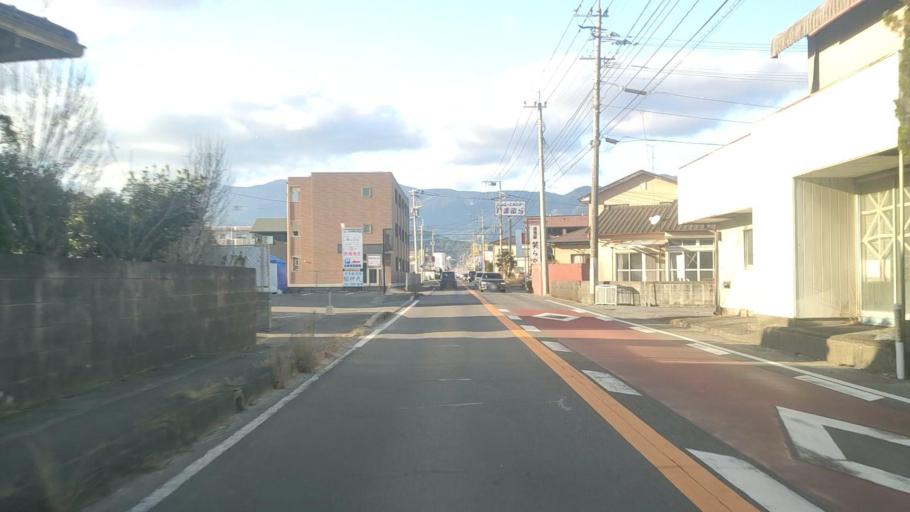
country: JP
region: Saga Prefecture
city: Saga-shi
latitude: 33.2825
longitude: 130.2109
